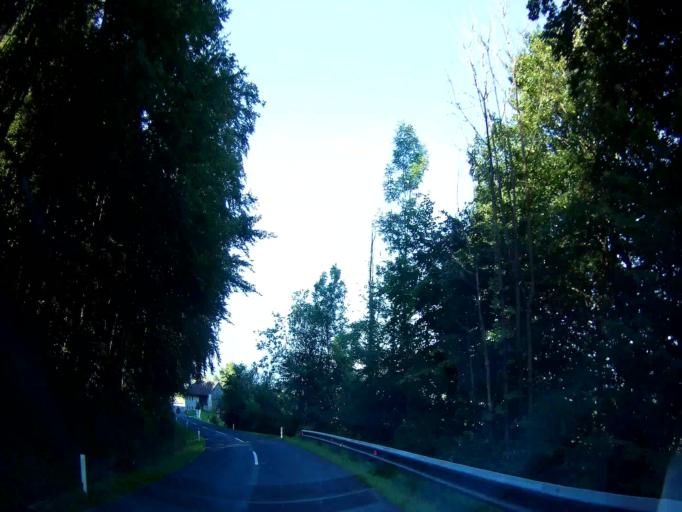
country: AT
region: Carinthia
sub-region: Politischer Bezirk Volkermarkt
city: Gallizien
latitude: 46.6016
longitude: 14.5309
